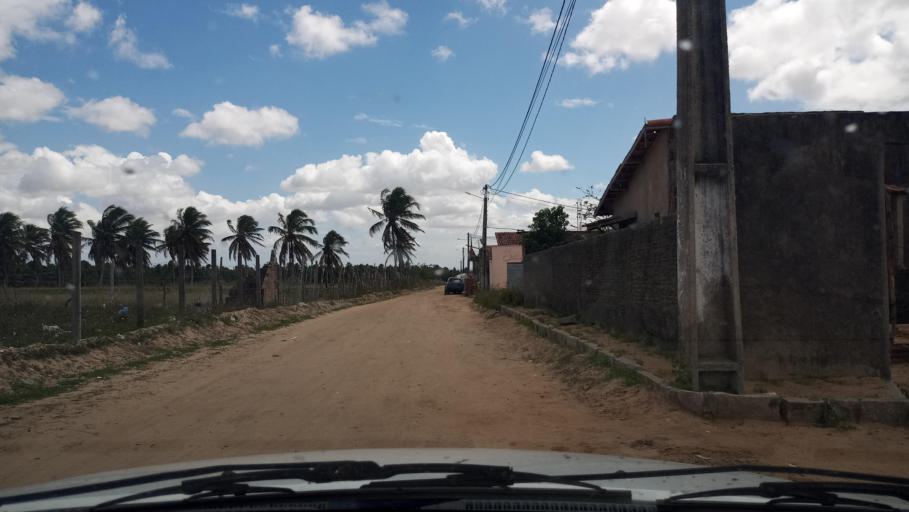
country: BR
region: Rio Grande do Norte
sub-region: Brejinho
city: Brejinho
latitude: -6.1929
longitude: -35.3638
